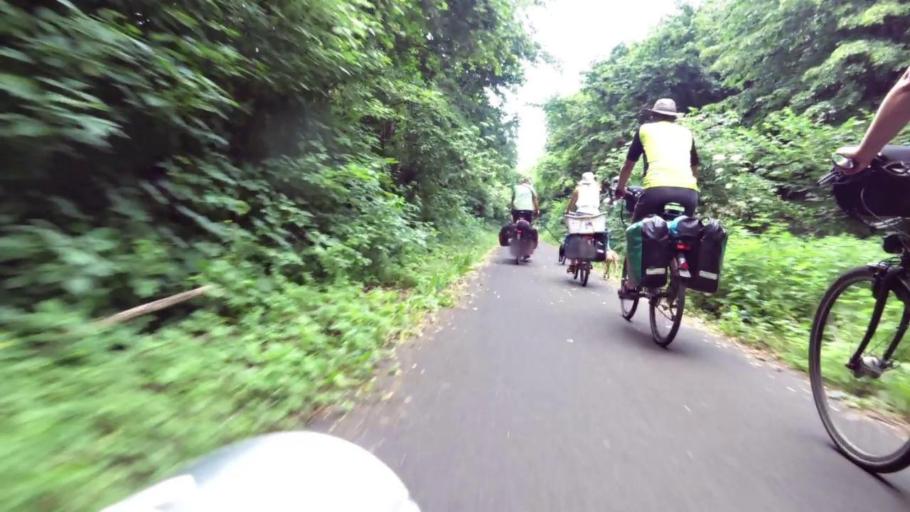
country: PL
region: Kujawsko-Pomorskie
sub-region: Powiat torunski
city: Lubianka
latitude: 53.0912
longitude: 18.5329
